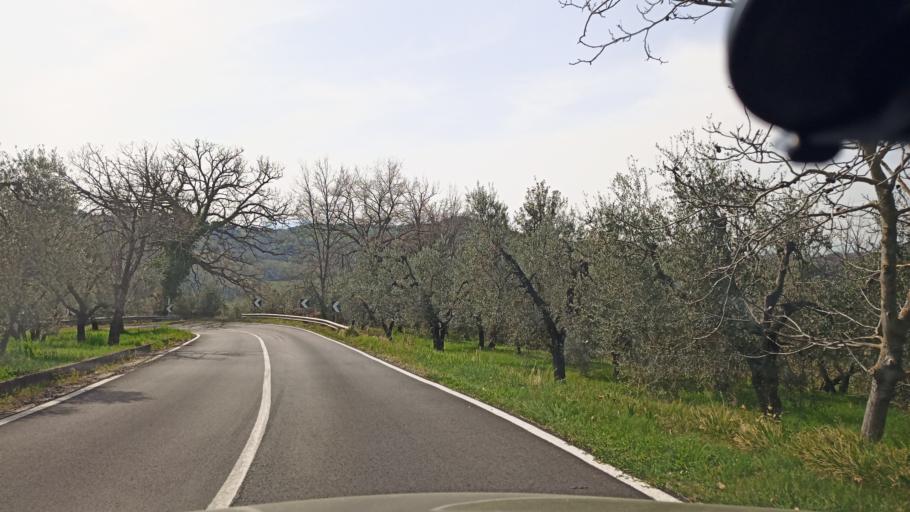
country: IT
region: Latium
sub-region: Provincia di Rieti
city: Torri in Sabina
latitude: 42.3302
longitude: 12.6446
